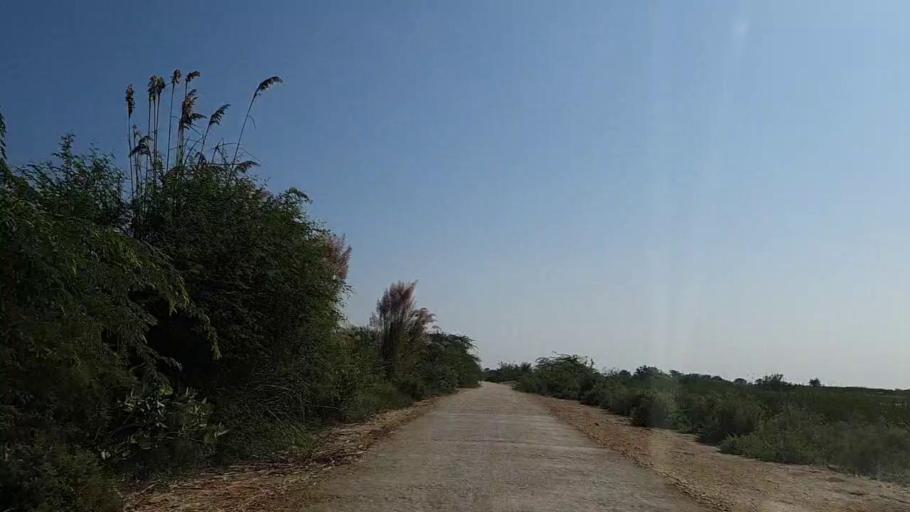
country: PK
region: Sindh
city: Chuhar Jamali
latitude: 24.4621
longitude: 68.1070
